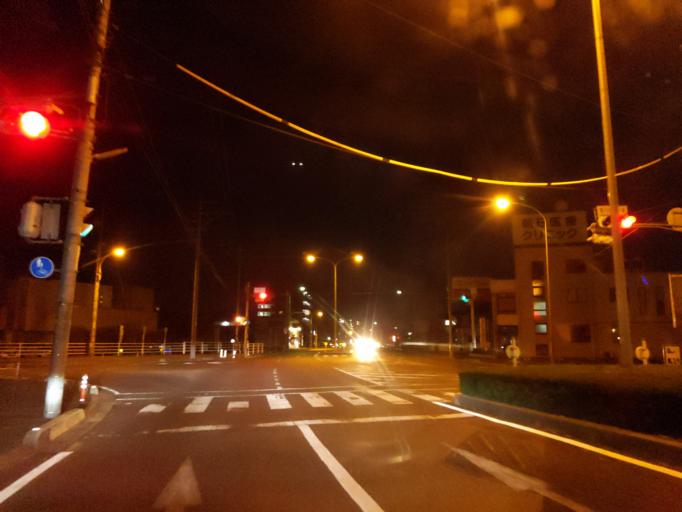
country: JP
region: Okayama
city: Okayama-shi
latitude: 34.6783
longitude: 133.9442
